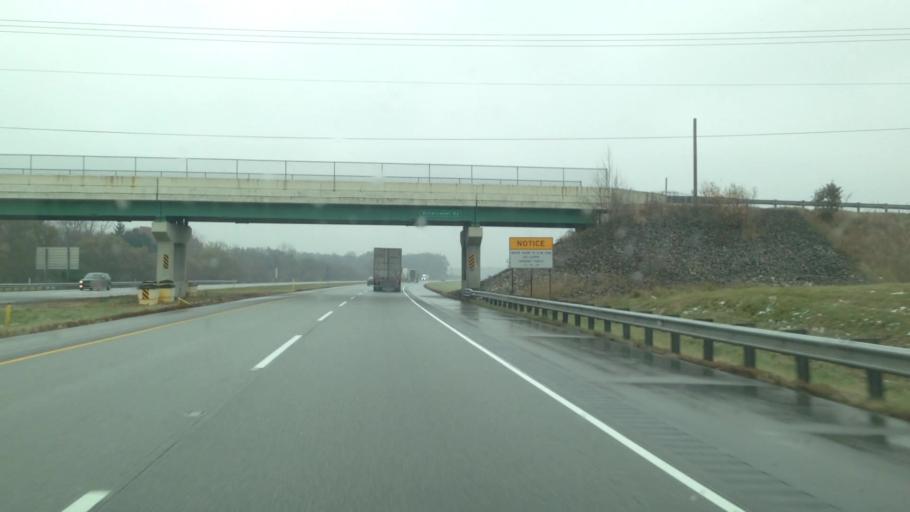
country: US
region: Indiana
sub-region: Saint Joseph County
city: Granger
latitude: 41.7337
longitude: -86.1115
